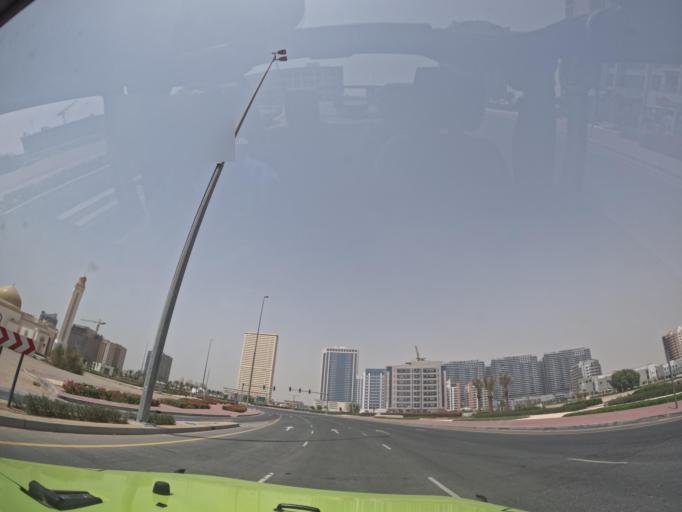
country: AE
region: Dubai
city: Dubai
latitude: 25.0900
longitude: 55.3797
